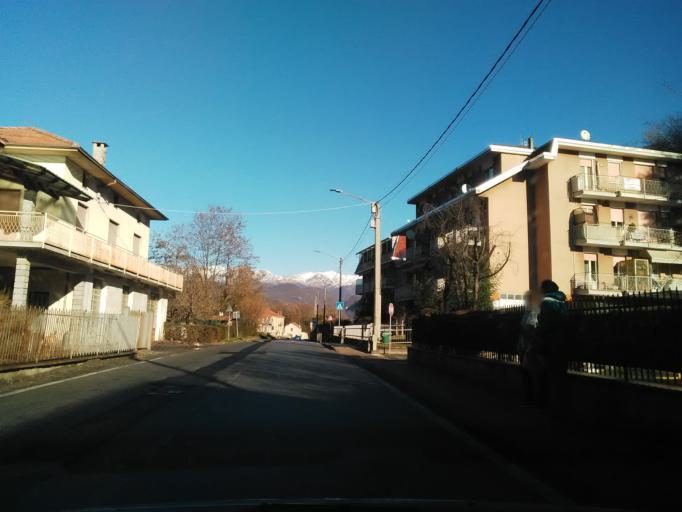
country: IT
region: Piedmont
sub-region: Provincia di Vercelli
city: Quarona
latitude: 45.7678
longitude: 8.2678
